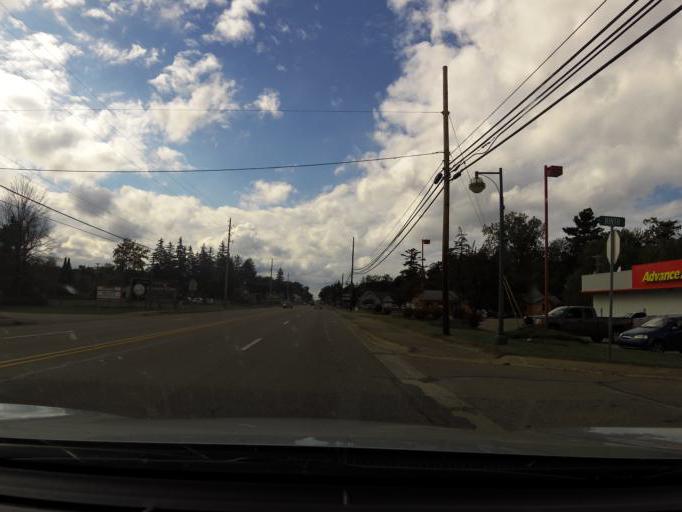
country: US
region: Michigan
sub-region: Roscommon County
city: Prudenville
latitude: 44.2985
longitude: -84.6599
